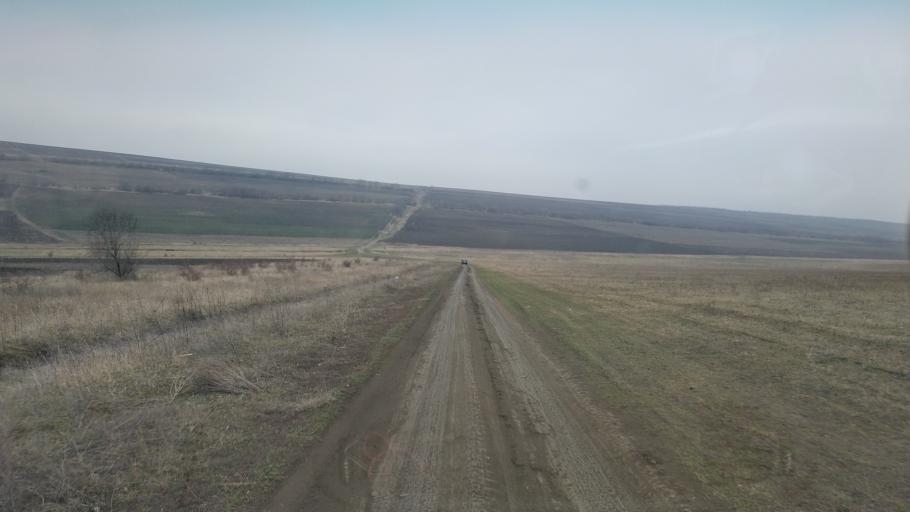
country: MD
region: Chisinau
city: Singera
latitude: 46.8269
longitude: 29.0154
